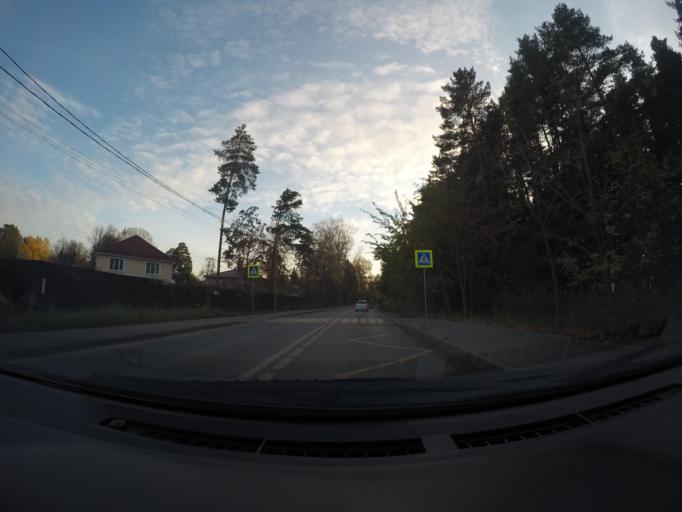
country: RU
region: Moskovskaya
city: Firsanovka
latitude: 55.9670
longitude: 37.2590
